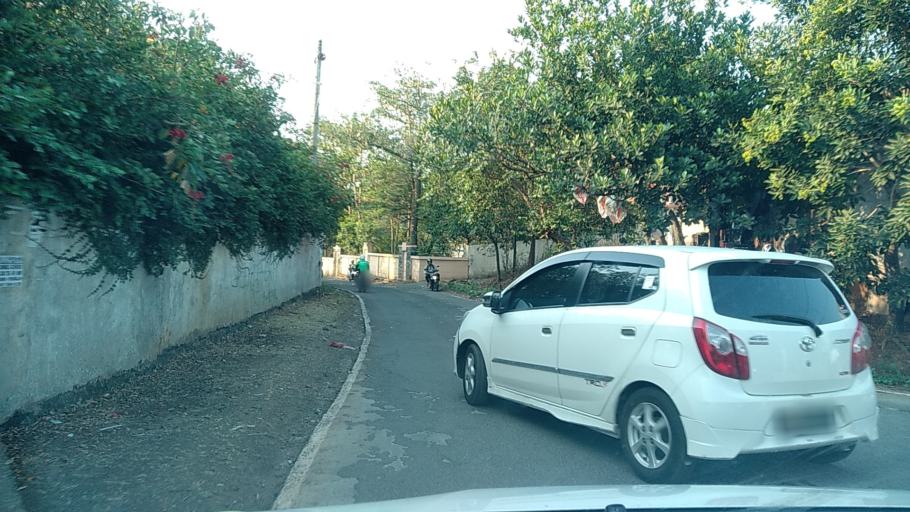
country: ID
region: Central Java
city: Semarang
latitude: -7.0564
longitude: 110.4434
